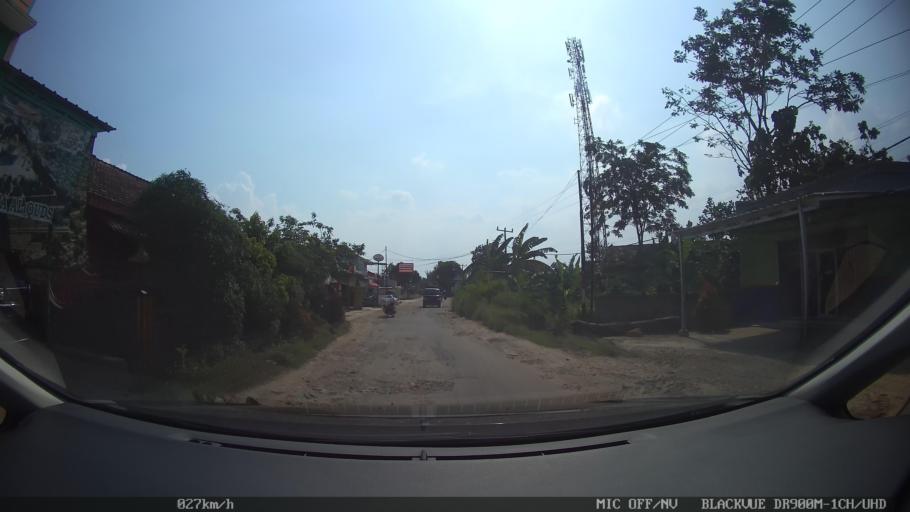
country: ID
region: Lampung
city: Natar
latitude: -5.3098
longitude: 105.2098
